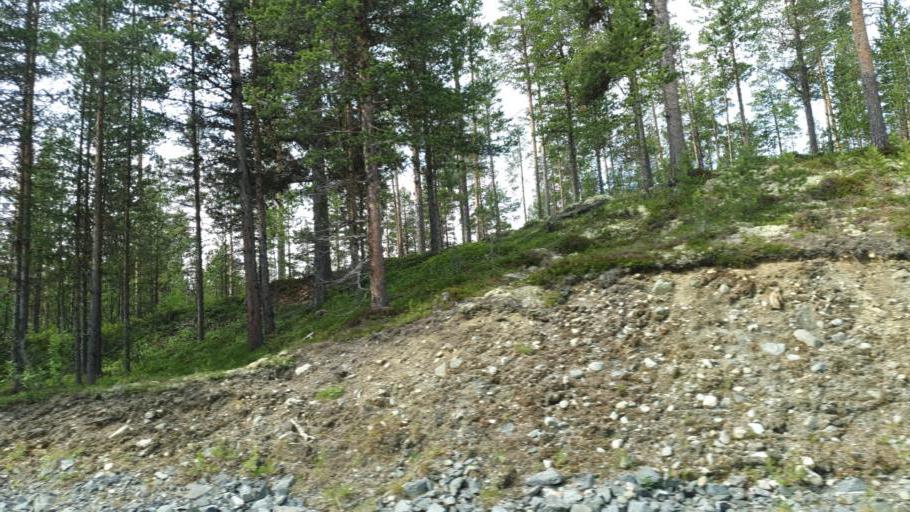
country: NO
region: Oppland
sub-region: Vaga
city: Vagamo
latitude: 61.7019
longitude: 9.0588
